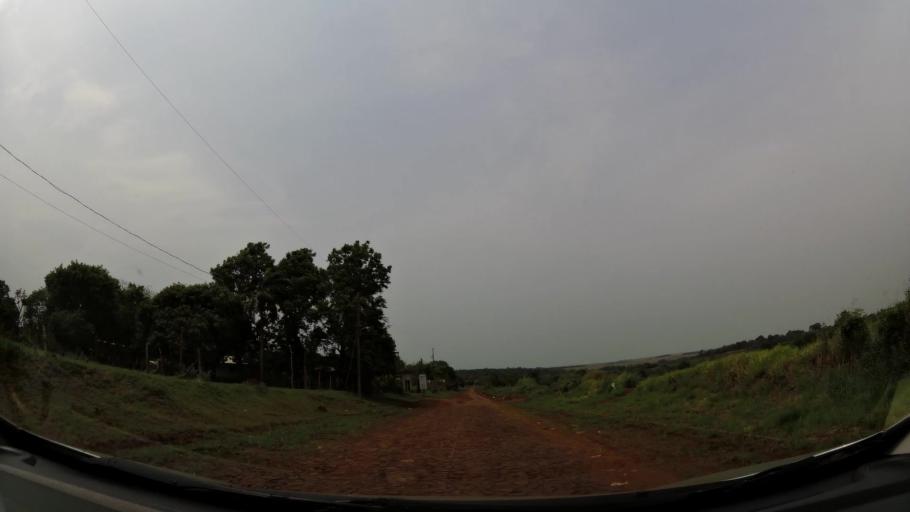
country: PY
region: Alto Parana
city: Presidente Franco
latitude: -25.5574
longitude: -54.6410
